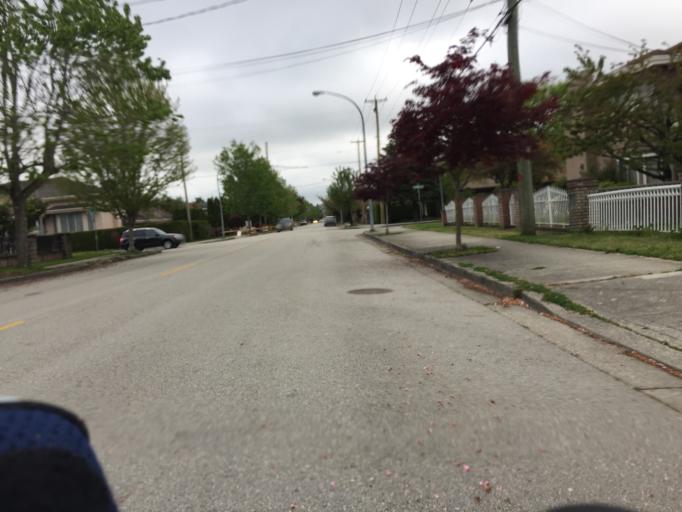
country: CA
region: British Columbia
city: Richmond
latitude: 49.1508
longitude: -123.1309
